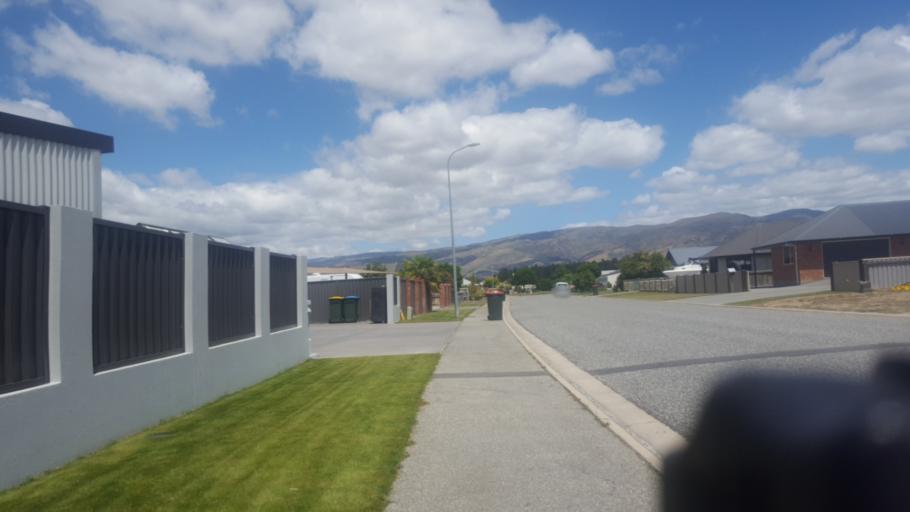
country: NZ
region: Otago
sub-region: Queenstown-Lakes District
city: Wanaka
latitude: -45.0497
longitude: 169.1990
